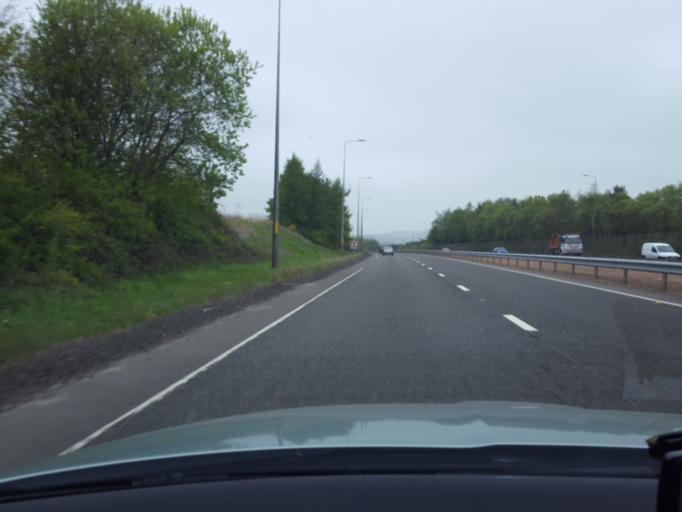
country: GB
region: Scotland
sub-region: Angus
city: Forfar
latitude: 56.5766
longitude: -2.9140
